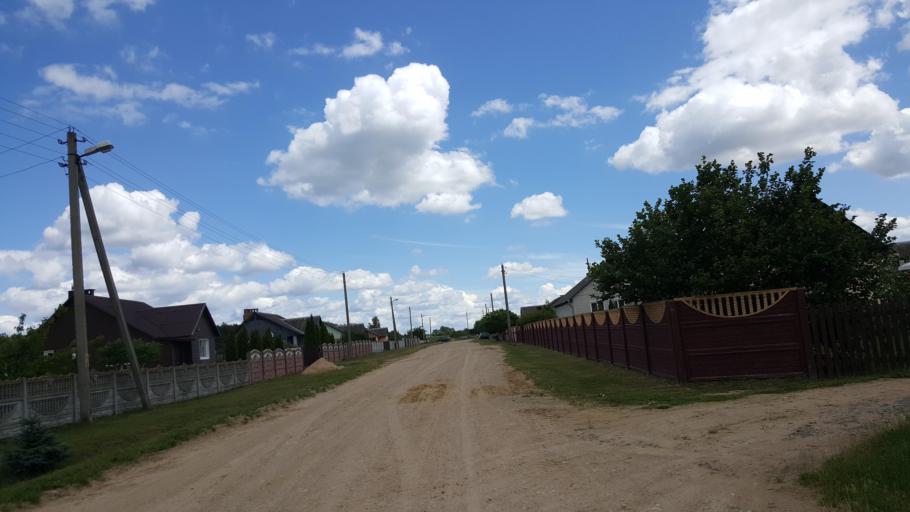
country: BY
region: Brest
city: Kamyanyets
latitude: 52.3221
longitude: 23.9268
